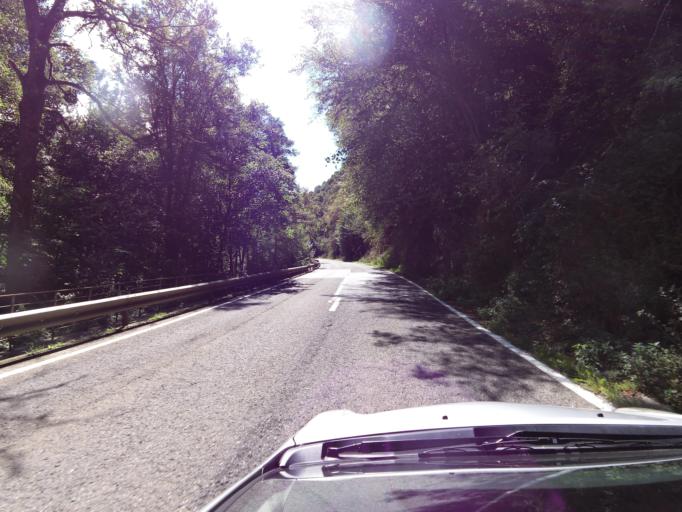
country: BE
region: Wallonia
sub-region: Province du Luxembourg
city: Rendeux
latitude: 50.2131
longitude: 5.5191
